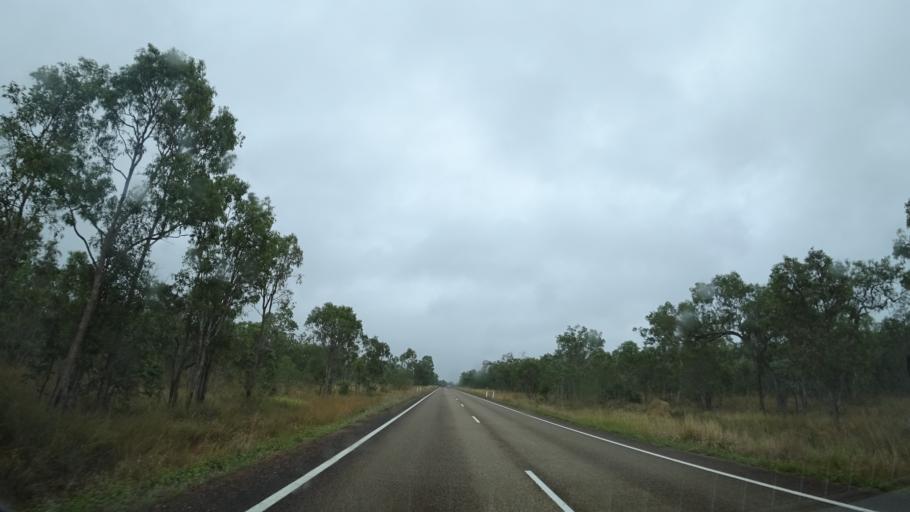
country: AU
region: Queensland
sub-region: Tablelands
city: Ravenshoe
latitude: -17.6892
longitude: 145.2255
